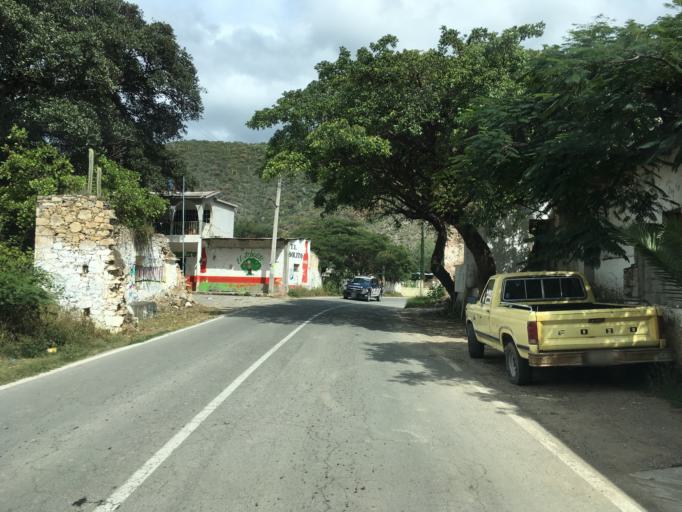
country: MX
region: Hidalgo
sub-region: San Agustin Metzquititlan
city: Mezquititlan
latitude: 20.5302
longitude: -98.7197
